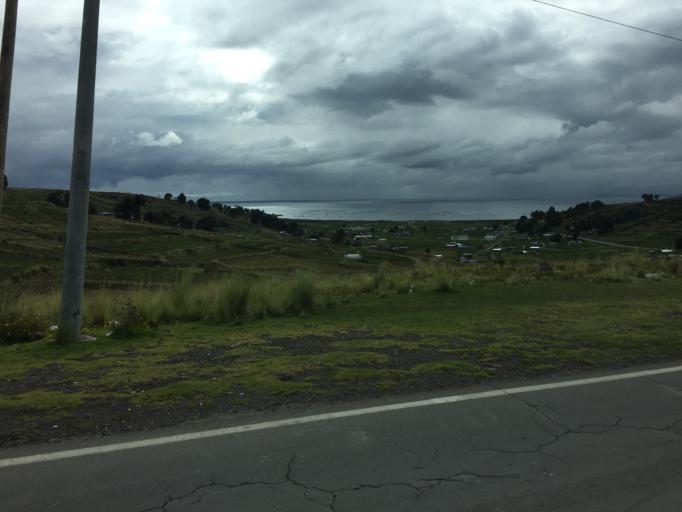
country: PE
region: Puno
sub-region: Provincia de Chucuito
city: Juli
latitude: -16.2036
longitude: -69.4166
